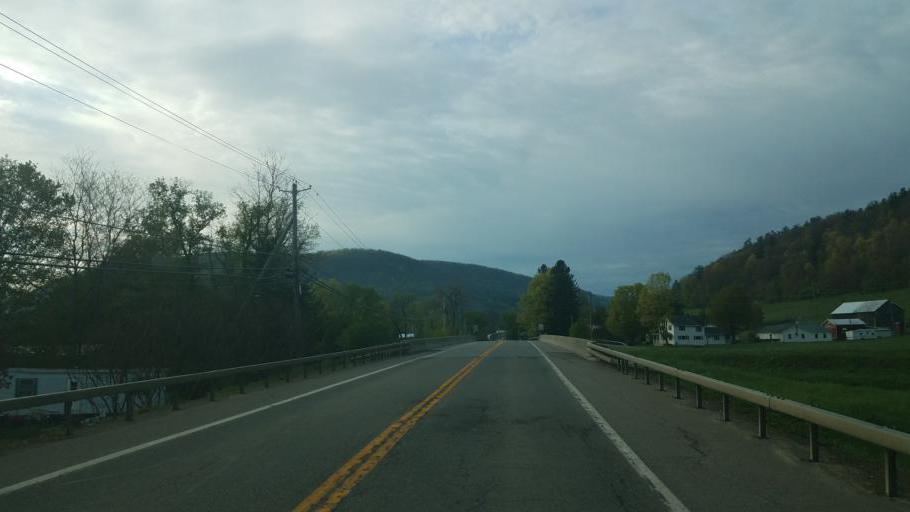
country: US
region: New York
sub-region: Steuben County
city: Canisteo
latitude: 42.2660
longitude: -77.5947
